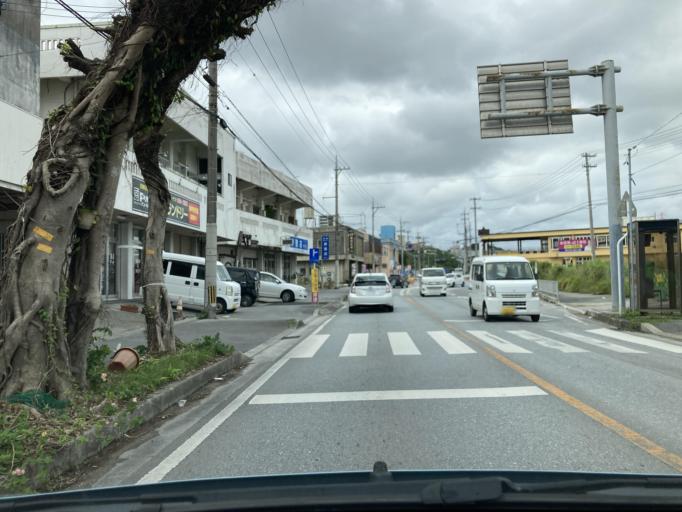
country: JP
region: Okinawa
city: Ginowan
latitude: 26.2392
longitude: 127.7457
